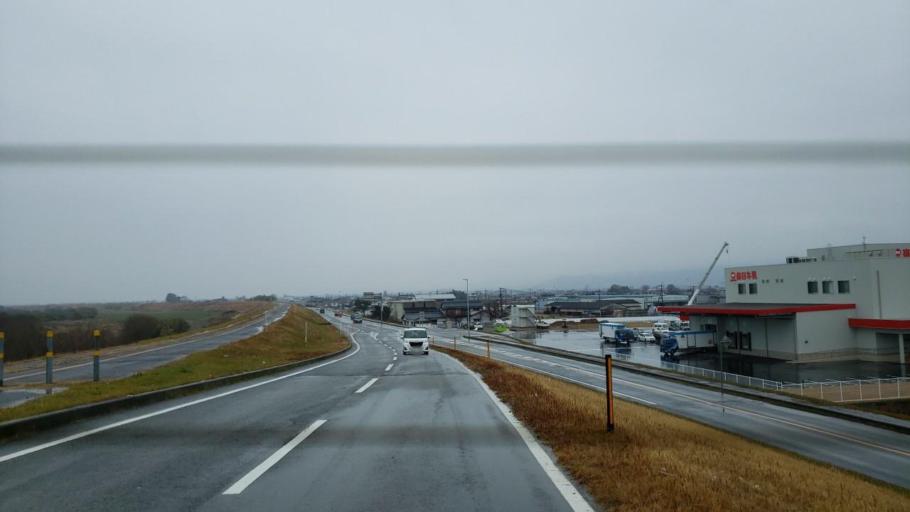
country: JP
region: Tokushima
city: Ishii
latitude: 34.1079
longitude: 134.4362
